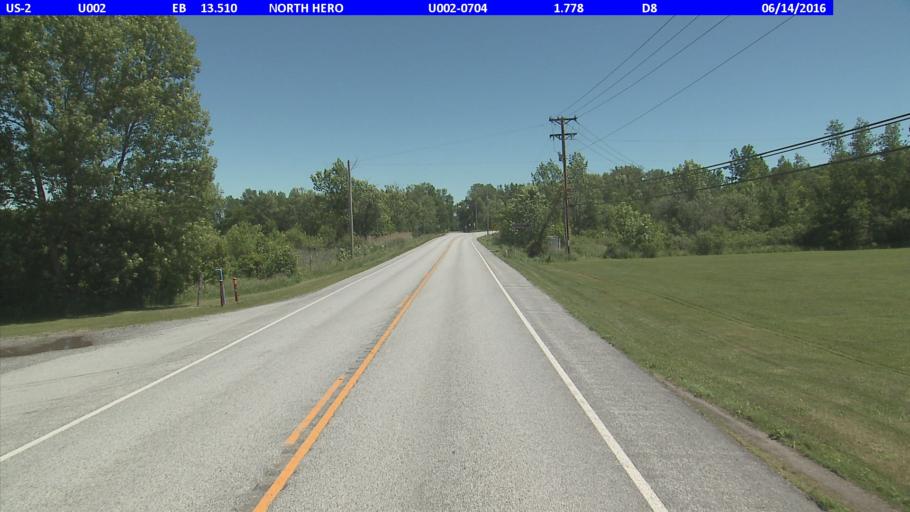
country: US
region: Vermont
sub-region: Grand Isle County
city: North Hero
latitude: 44.8632
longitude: -73.2625
